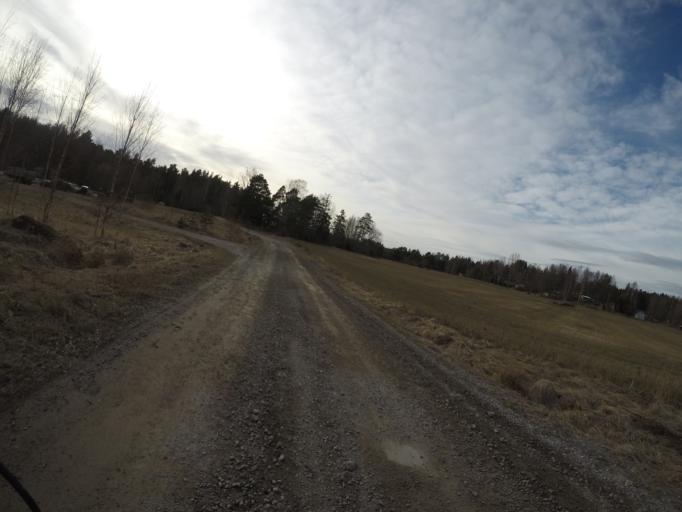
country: SE
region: Soedermanland
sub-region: Eskilstuna Kommun
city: Hallbybrunn
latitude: 59.4297
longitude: 16.4174
